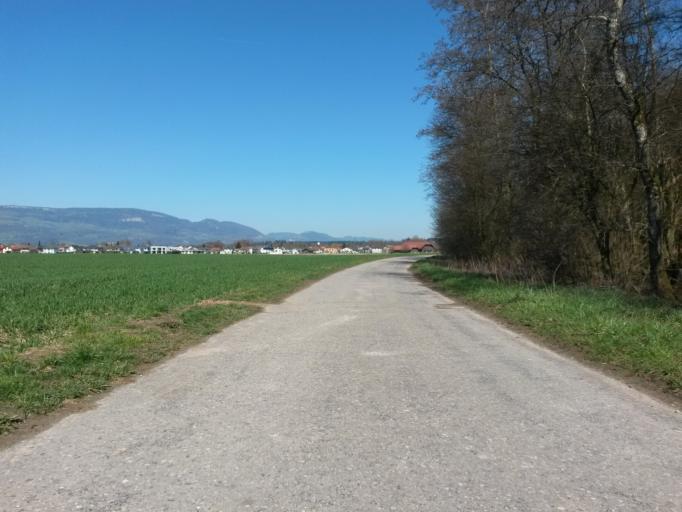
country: CH
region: Solothurn
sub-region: Bezirk Wasseramt
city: Kriegstetten
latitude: 47.1850
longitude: 7.6087
